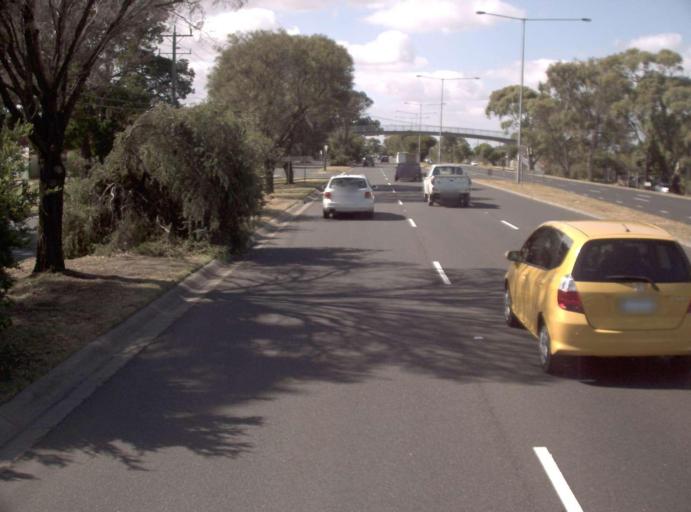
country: AU
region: Victoria
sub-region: Kingston
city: Parkdale
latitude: -37.9910
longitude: 145.0817
